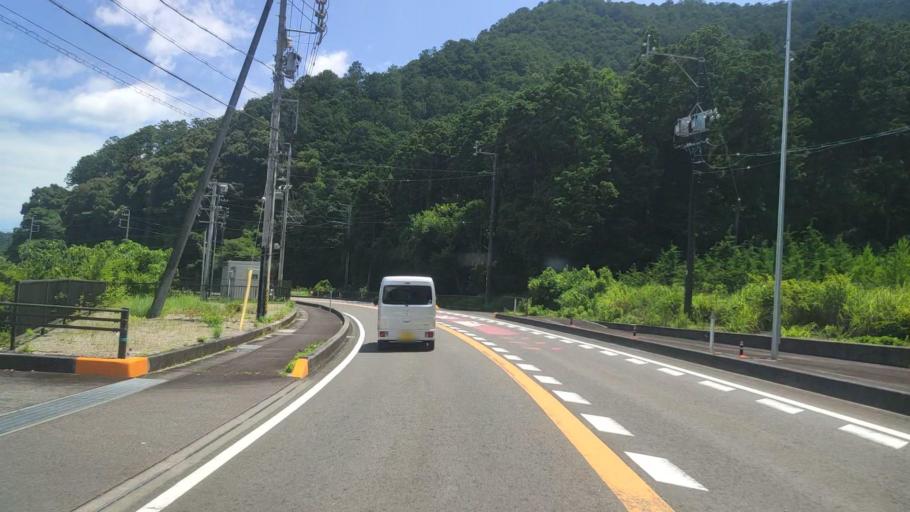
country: JP
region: Mie
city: Owase
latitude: 34.1155
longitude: 136.2200
